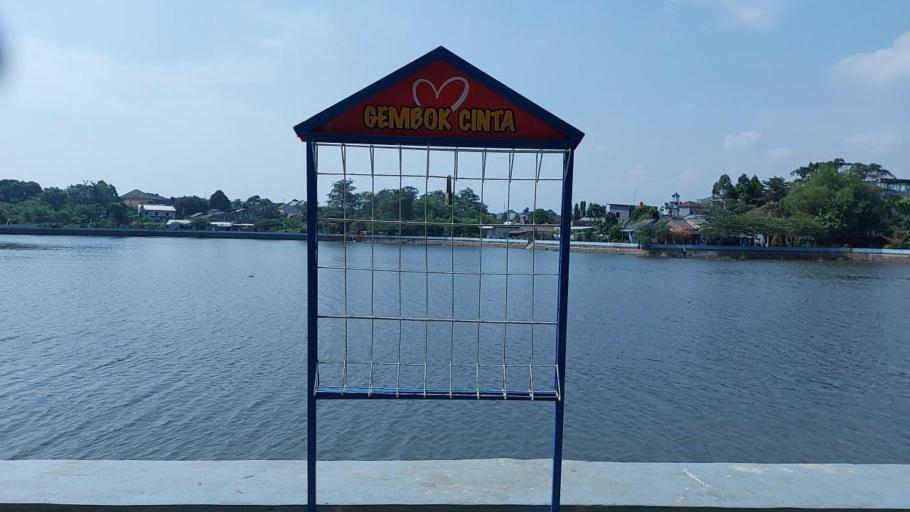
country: ID
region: West Java
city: Cibinong
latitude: -6.4713
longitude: 106.8553
